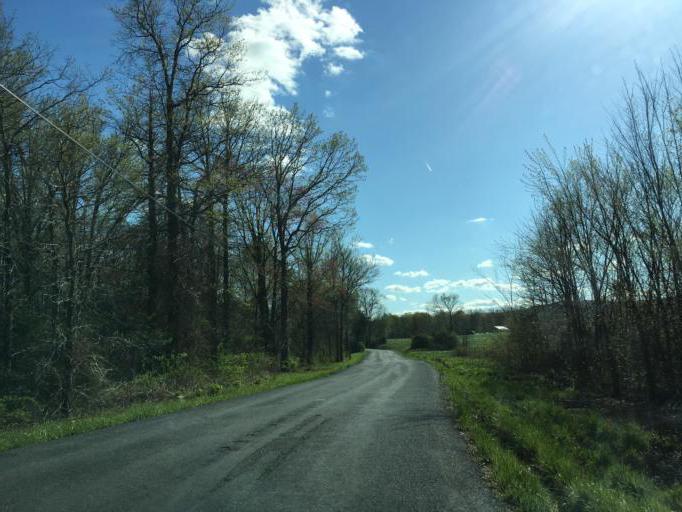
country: US
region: Maryland
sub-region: Frederick County
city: Thurmont
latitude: 39.6474
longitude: -77.3865
